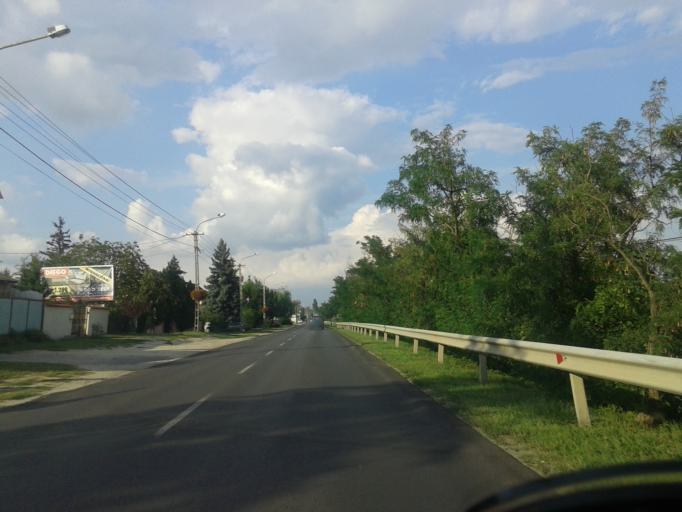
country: HU
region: Pest
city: Dunaharaszti
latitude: 47.3733
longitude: 19.0986
